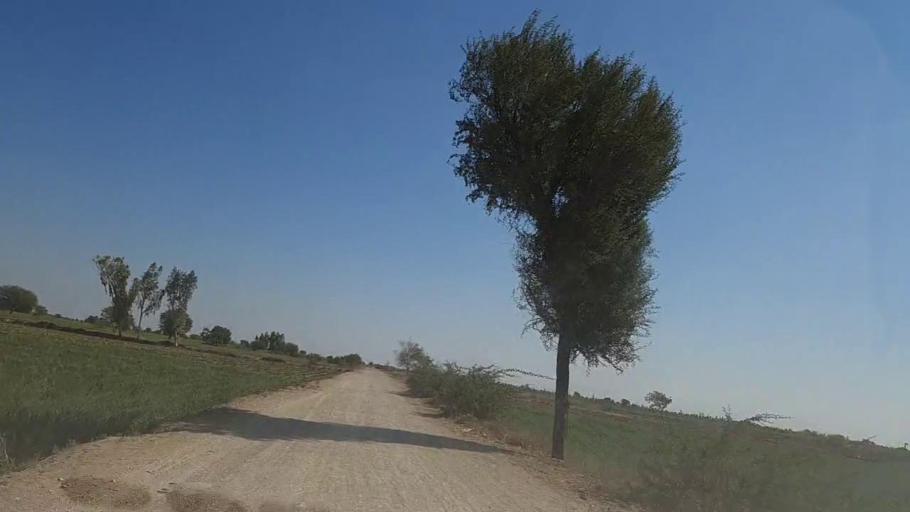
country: PK
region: Sindh
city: Digri
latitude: 25.1116
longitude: 69.1171
